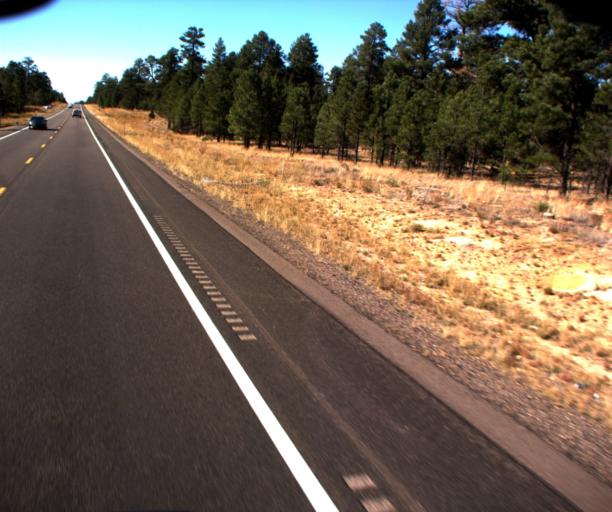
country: US
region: Arizona
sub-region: Apache County
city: Saint Michaels
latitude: 35.6920
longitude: -109.2608
